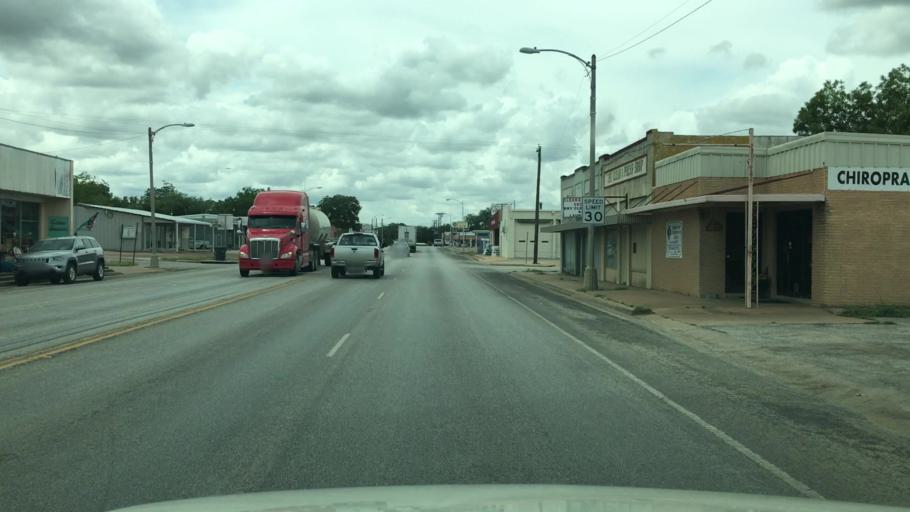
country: US
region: Texas
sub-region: McCulloch County
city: Brady
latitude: 31.1349
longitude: -99.3369
